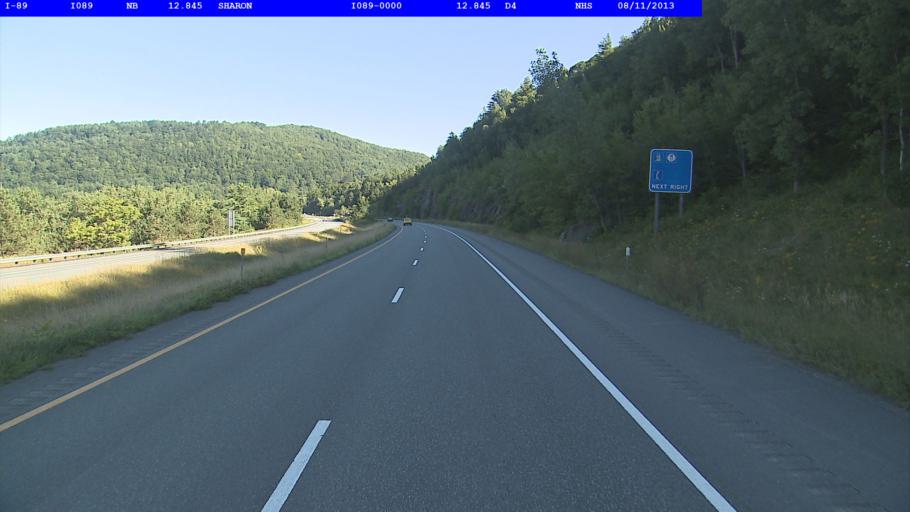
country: US
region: Vermont
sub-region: Windsor County
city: Woodstock
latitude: 43.7802
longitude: -72.4451
